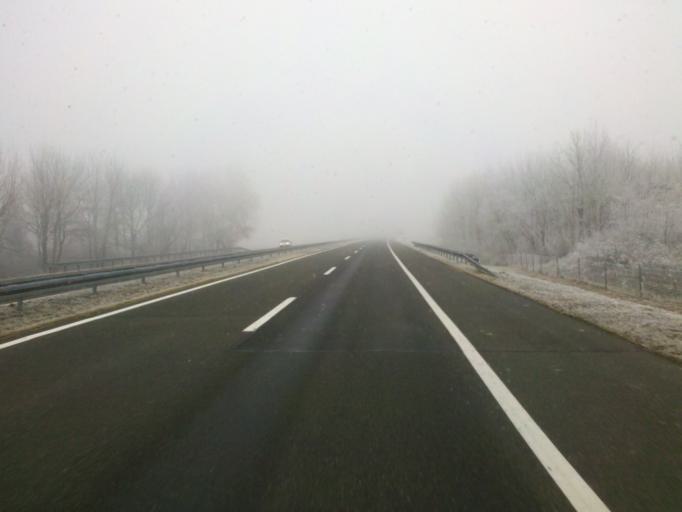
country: HR
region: Medimurska
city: Orehovica
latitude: 46.3182
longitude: 16.5122
